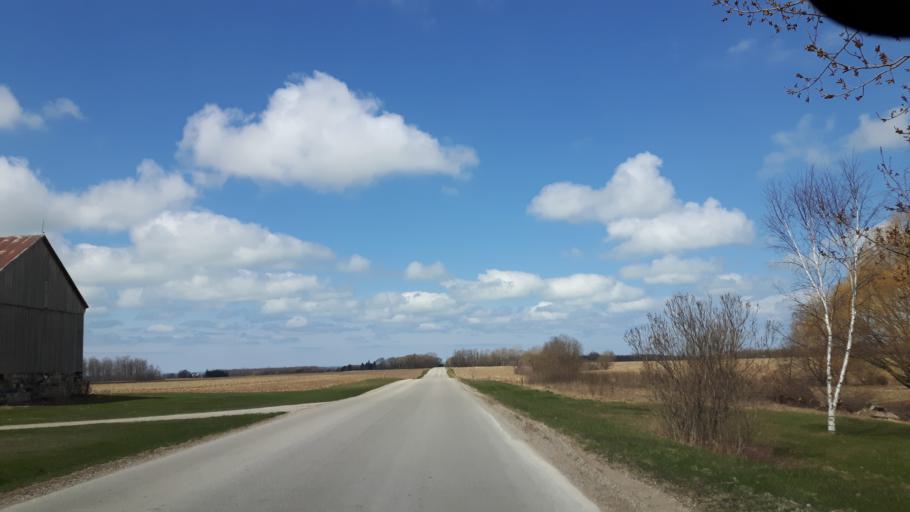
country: CA
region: Ontario
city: Goderich
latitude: 43.6985
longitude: -81.6851
